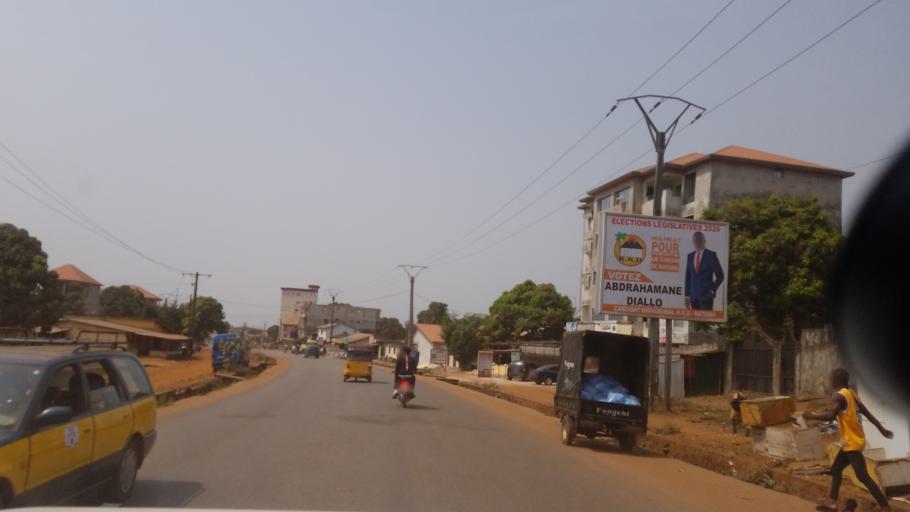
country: GN
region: Kindia
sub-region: Prefecture de Dubreka
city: Dubreka
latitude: 9.6789
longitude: -13.5676
